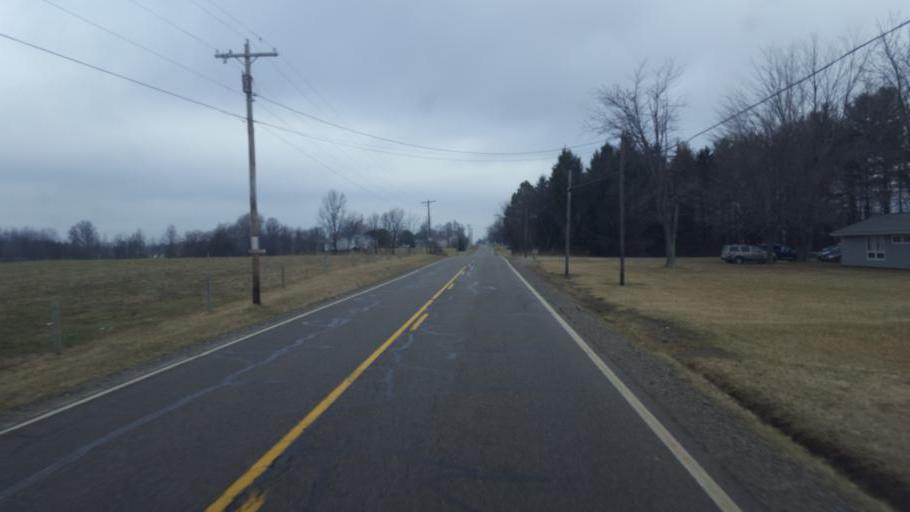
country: US
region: Ohio
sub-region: Richland County
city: Lexington
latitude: 40.6767
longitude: -82.6641
